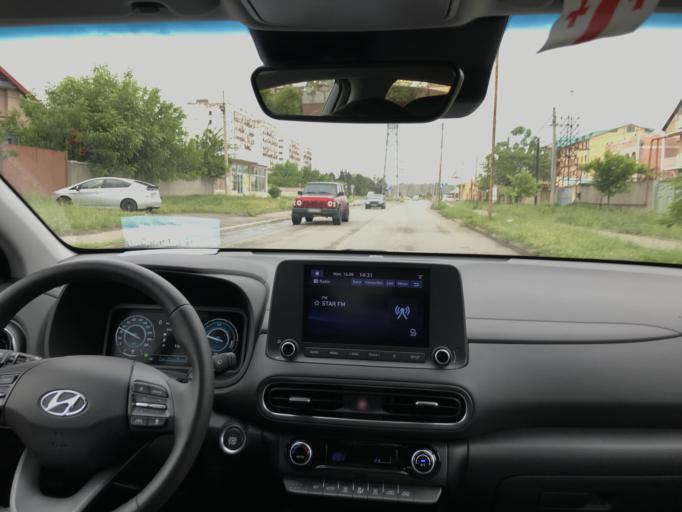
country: GE
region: Kvemo Kartli
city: Rust'avi
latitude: 41.5626
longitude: 44.9947
